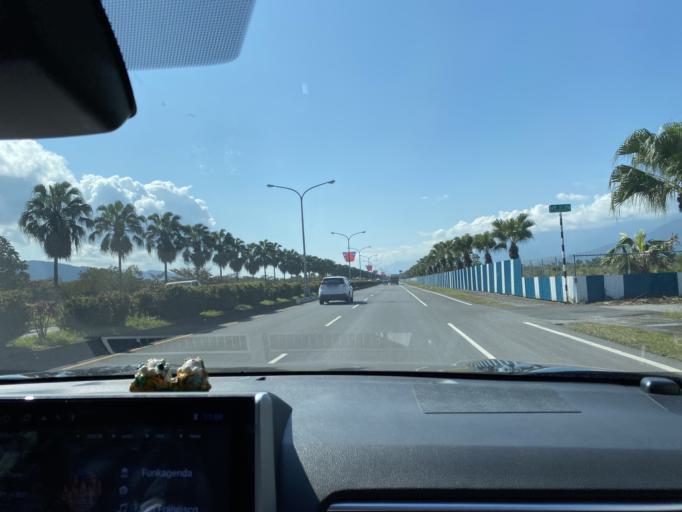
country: TW
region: Taiwan
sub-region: Hualien
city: Hualian
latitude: 23.8718
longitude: 121.5362
